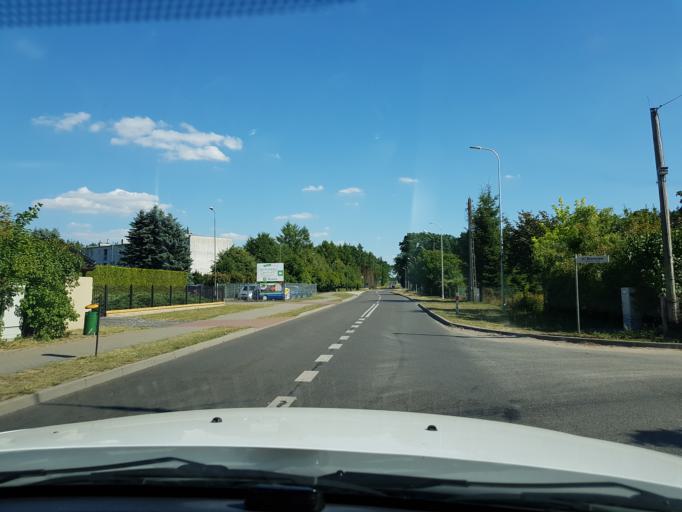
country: PL
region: West Pomeranian Voivodeship
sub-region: Powiat swidwinski
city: Slawoborze
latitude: 53.8884
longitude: 15.7153
